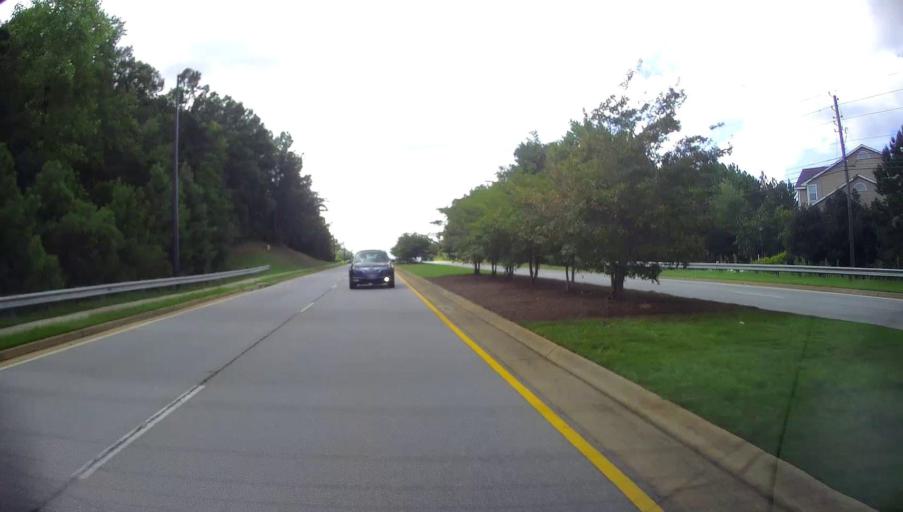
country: US
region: Alabama
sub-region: Russell County
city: Phenix City
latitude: 32.5605
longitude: -84.9323
